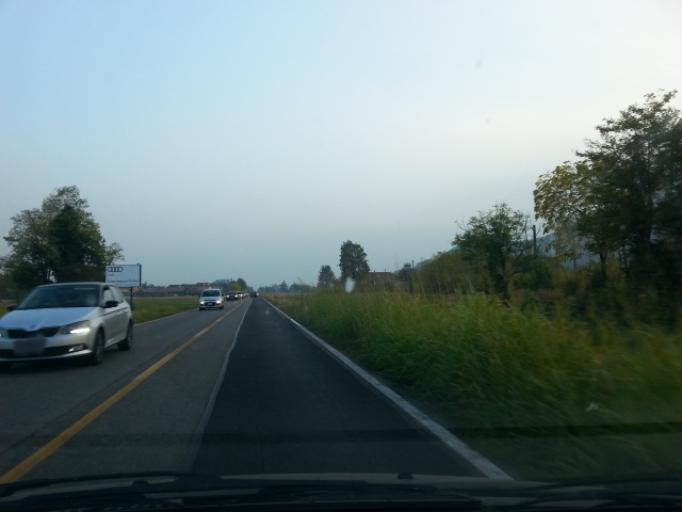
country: IT
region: Piedmont
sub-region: Provincia di Torino
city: Bruino
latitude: 45.0123
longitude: 7.4657
